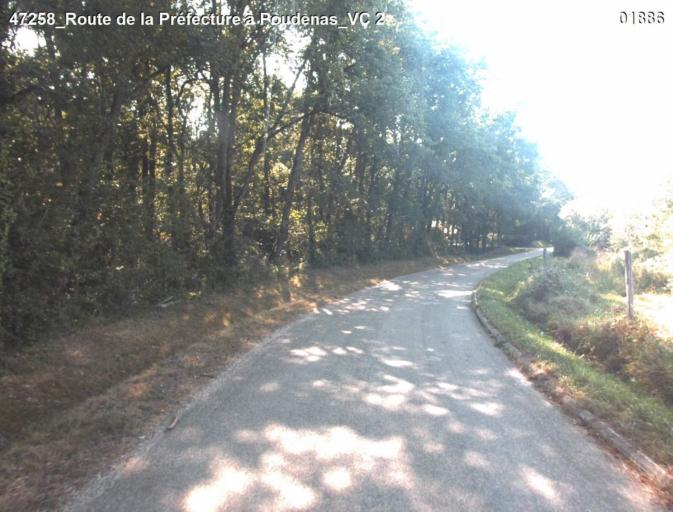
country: FR
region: Midi-Pyrenees
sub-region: Departement du Gers
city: Montreal
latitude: 44.0251
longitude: 0.1795
